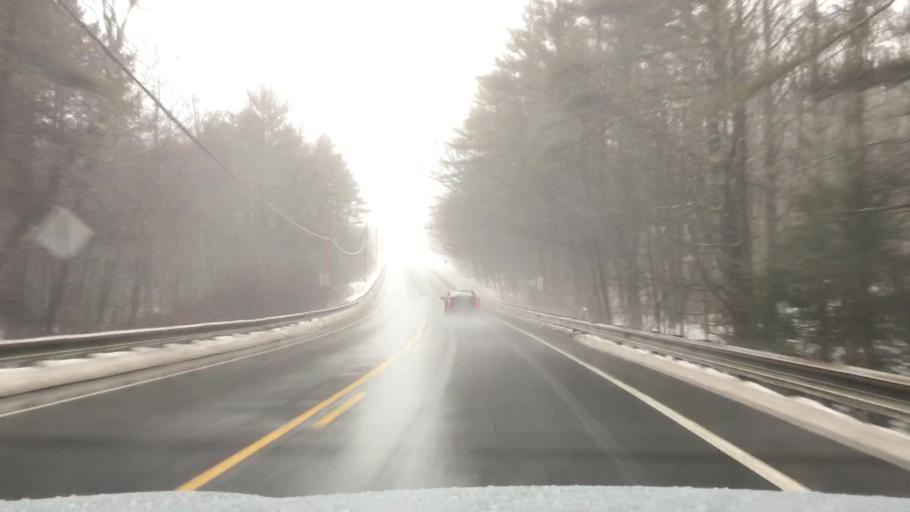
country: US
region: Massachusetts
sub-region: Franklin County
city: Orange
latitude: 42.5387
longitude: -72.3029
